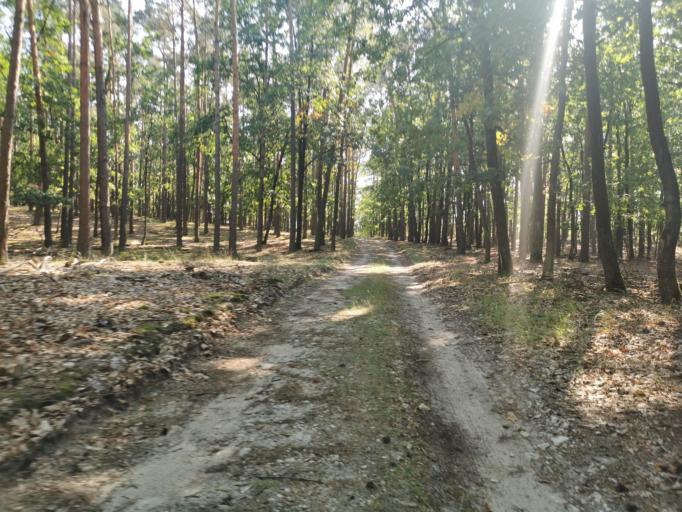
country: SK
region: Trnavsky
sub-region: Okres Senica
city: Senica
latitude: 48.6257
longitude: 17.2817
